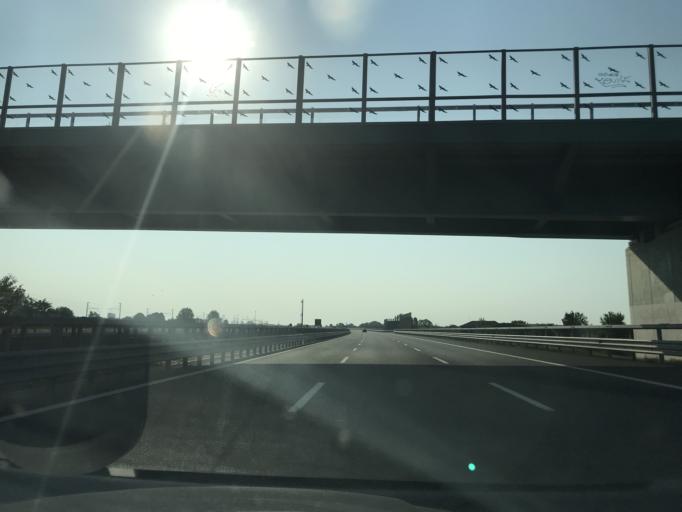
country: IT
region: Lombardy
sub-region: Provincia di Bergamo
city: Casirate d'Adda
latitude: 45.5041
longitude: 9.5789
